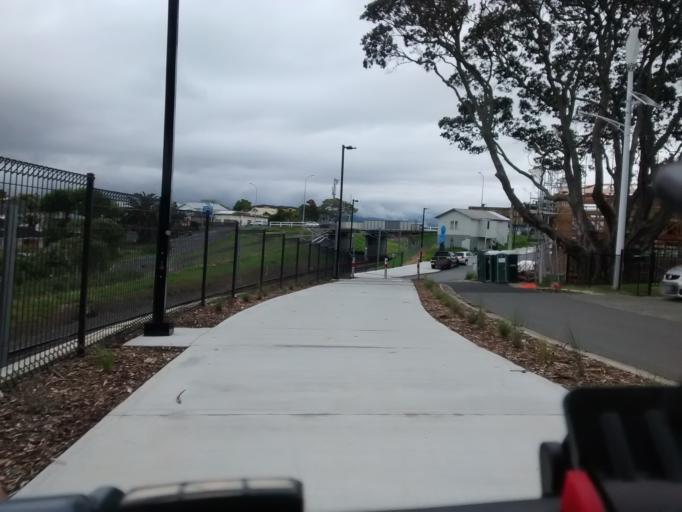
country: NZ
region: Auckland
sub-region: Auckland
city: Rosebank
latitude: -36.8939
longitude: 174.7022
